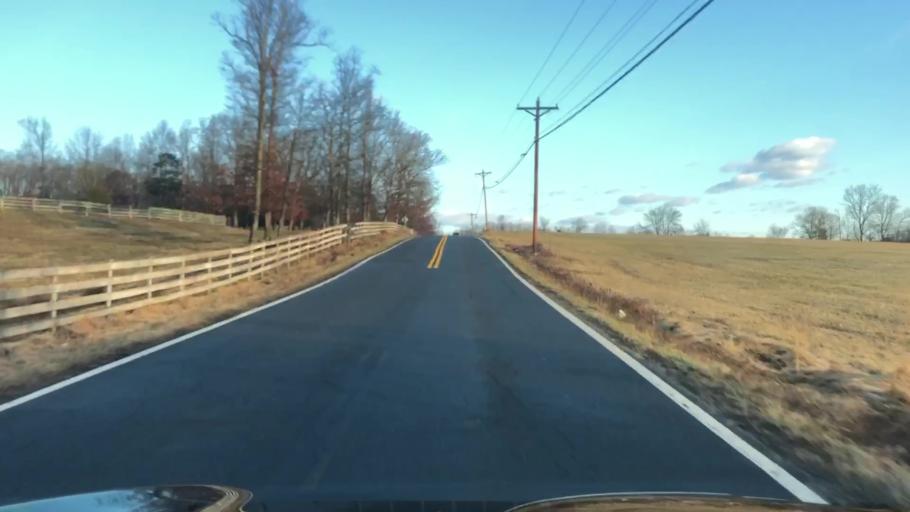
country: US
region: Virginia
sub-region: Fauquier County
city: Bealeton
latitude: 38.5645
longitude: -77.6753
